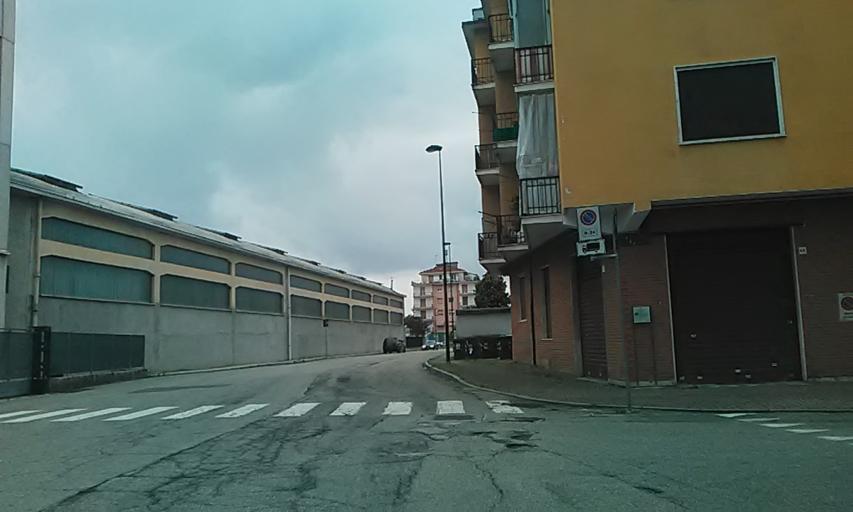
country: IT
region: Piedmont
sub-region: Provincia di Alessandria
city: Casale Monferrato
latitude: 45.1474
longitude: 8.4428
